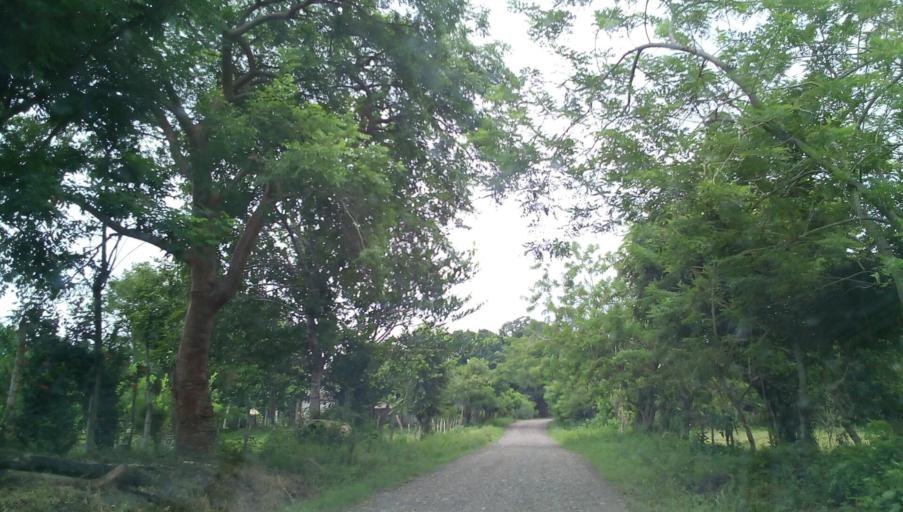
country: MX
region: Veracruz
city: Tepetzintla
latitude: 21.1246
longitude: -97.8560
